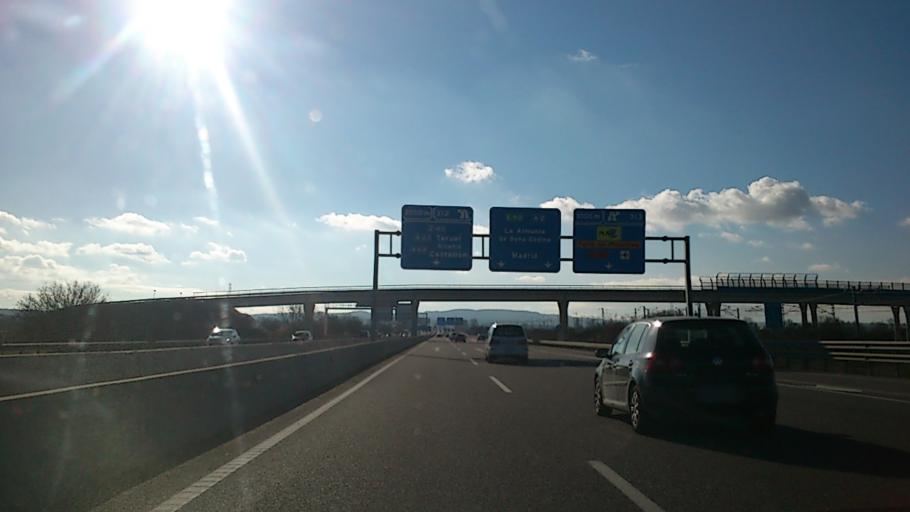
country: ES
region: Aragon
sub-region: Provincia de Zaragoza
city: Oliver-Valdefierro, Oliver, Valdefierro
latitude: 41.6541
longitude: -0.9576
